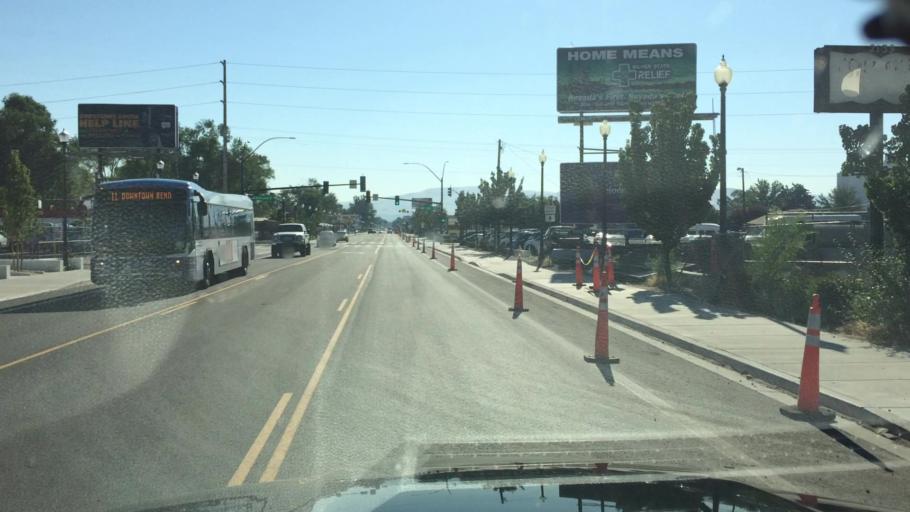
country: US
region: Nevada
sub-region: Washoe County
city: Sparks
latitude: 39.5365
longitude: -119.7726
